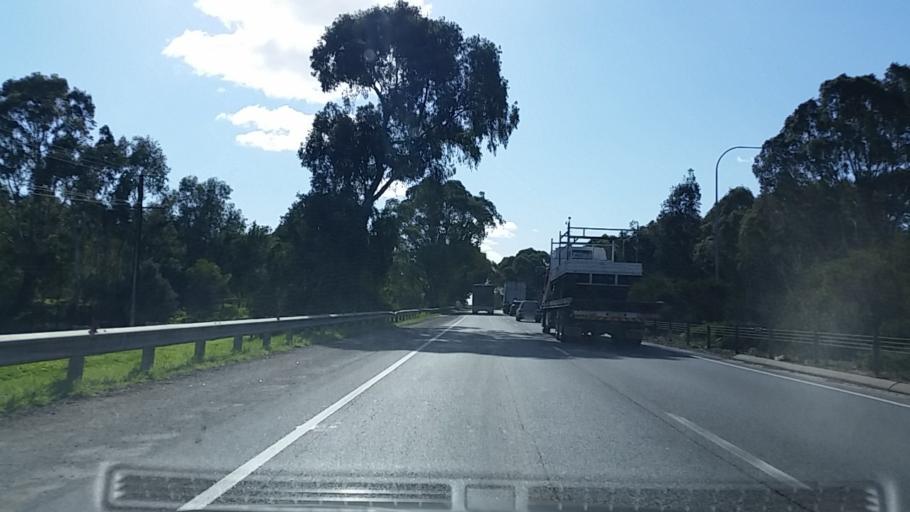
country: AU
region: South Australia
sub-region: Salisbury
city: Salisbury
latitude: -34.7733
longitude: 138.5946
